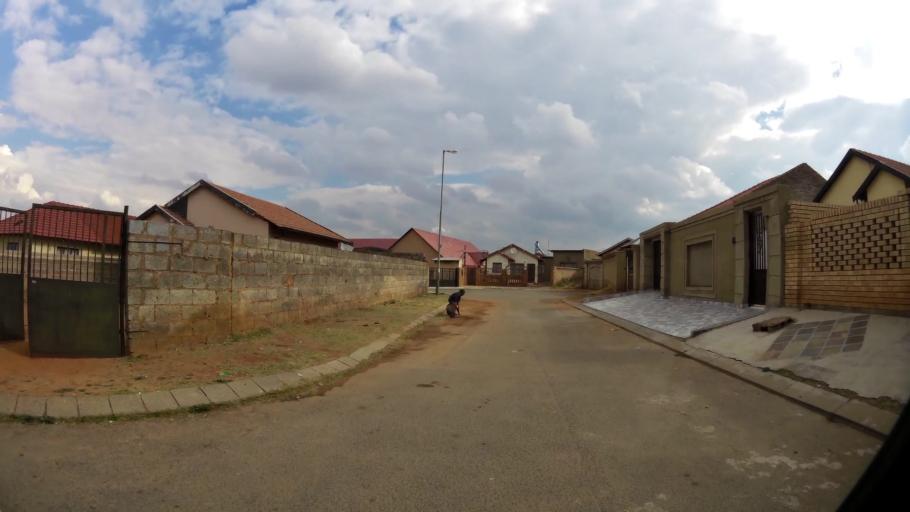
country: ZA
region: Gauteng
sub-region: City of Johannesburg Metropolitan Municipality
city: Soweto
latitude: -26.2356
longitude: 27.8702
